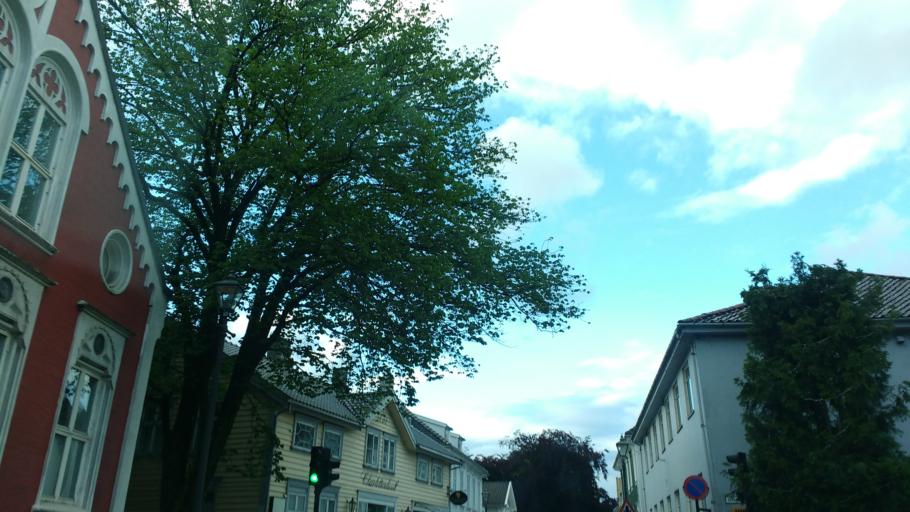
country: NO
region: Rogaland
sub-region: Stavanger
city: Stavanger
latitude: 58.9674
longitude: 5.7346
